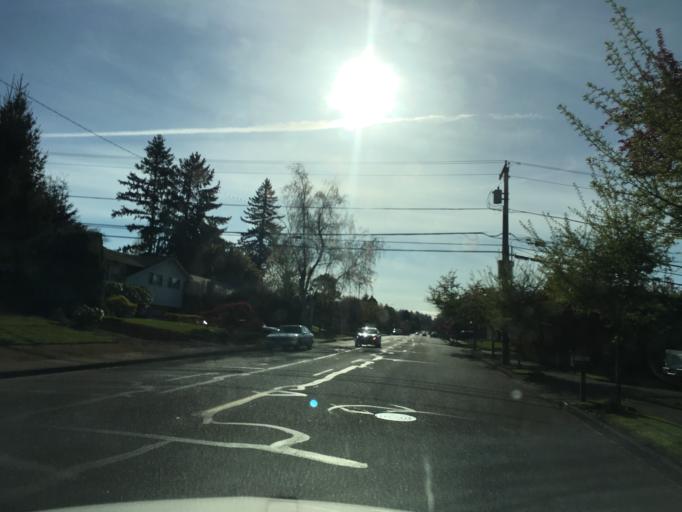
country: US
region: Oregon
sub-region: Multnomah County
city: Lents
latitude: 45.5482
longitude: -122.5242
